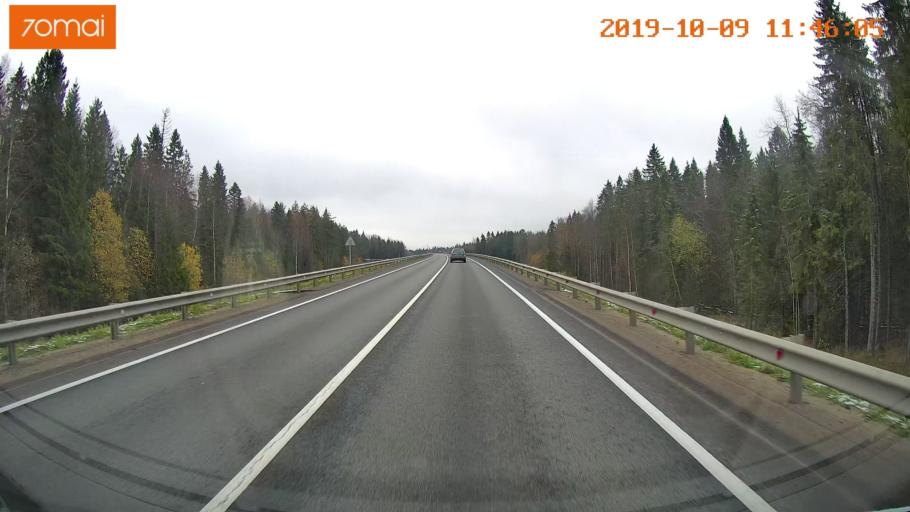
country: RU
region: Vologda
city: Gryazovets
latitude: 58.8594
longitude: 40.1993
